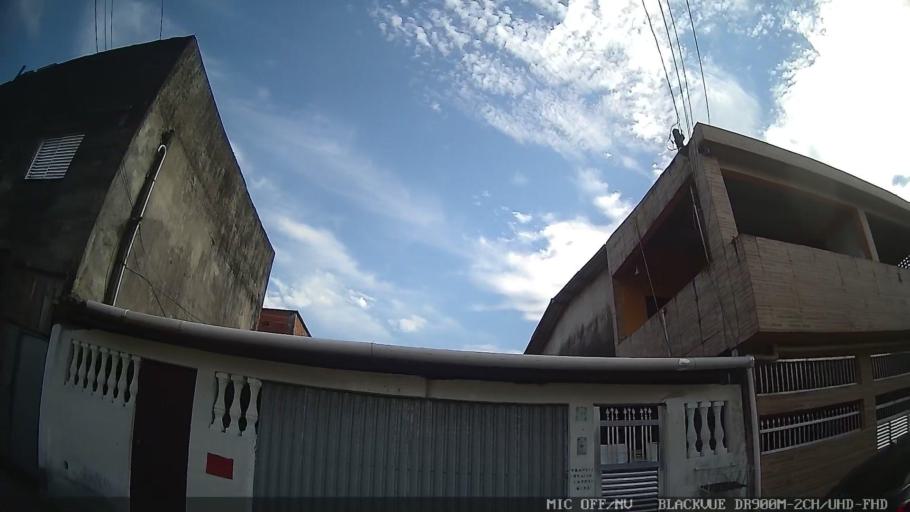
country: BR
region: Sao Paulo
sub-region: Guaruja
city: Guaruja
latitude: -23.9625
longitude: -46.2564
